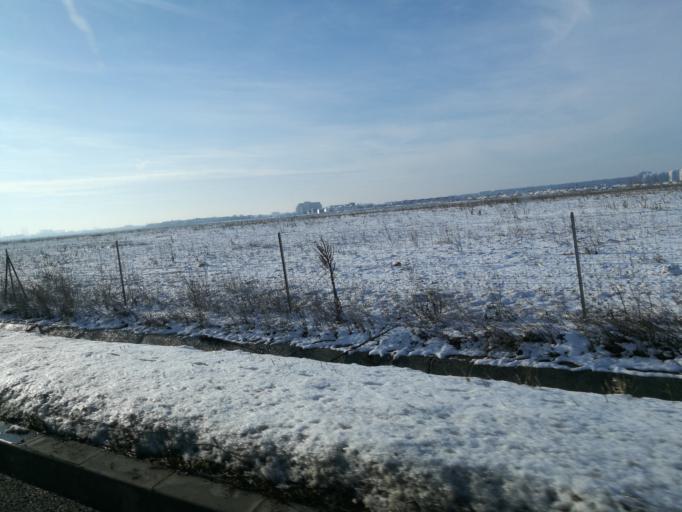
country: RO
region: Ilfov
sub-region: Voluntari City
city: Voluntari
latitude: 44.5151
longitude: 26.1676
